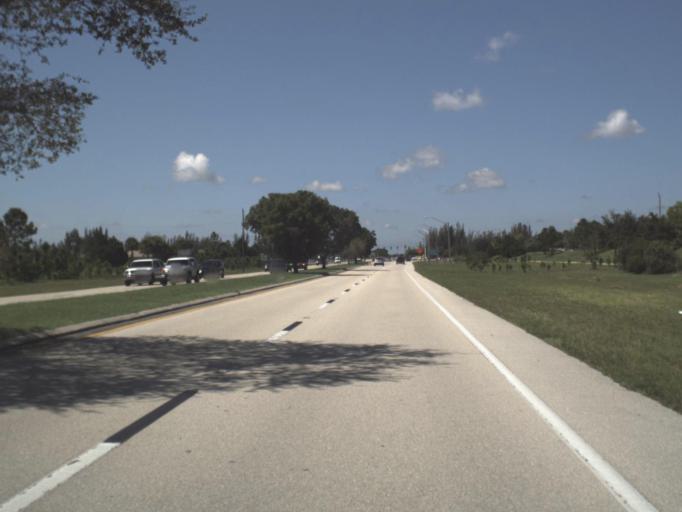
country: US
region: Florida
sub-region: Lee County
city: Cape Coral
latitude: 26.6071
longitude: -82.0024
